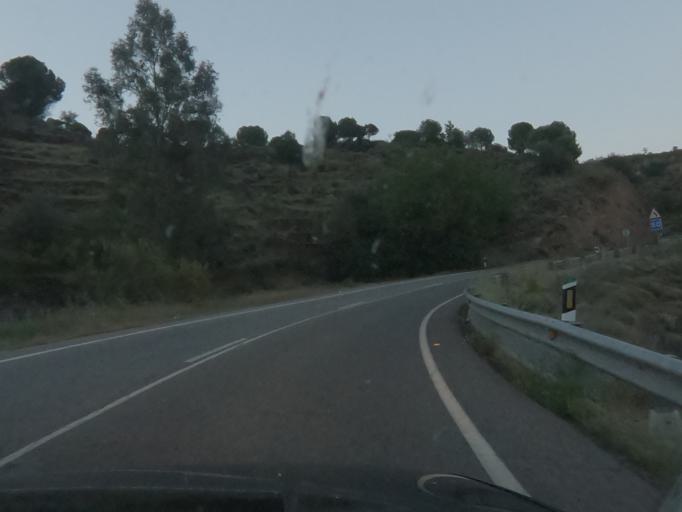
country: ES
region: Extremadura
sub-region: Provincia de Caceres
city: Alcantara
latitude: 39.7257
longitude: -6.8933
